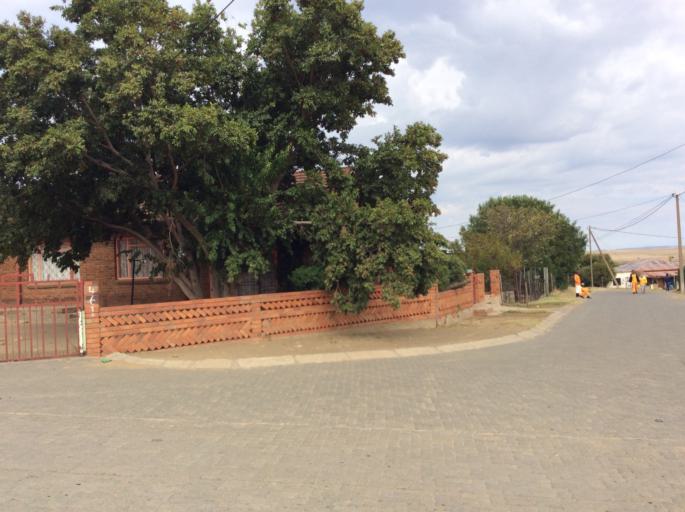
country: LS
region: Mafeteng
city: Mafeteng
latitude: -29.7200
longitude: 27.0281
